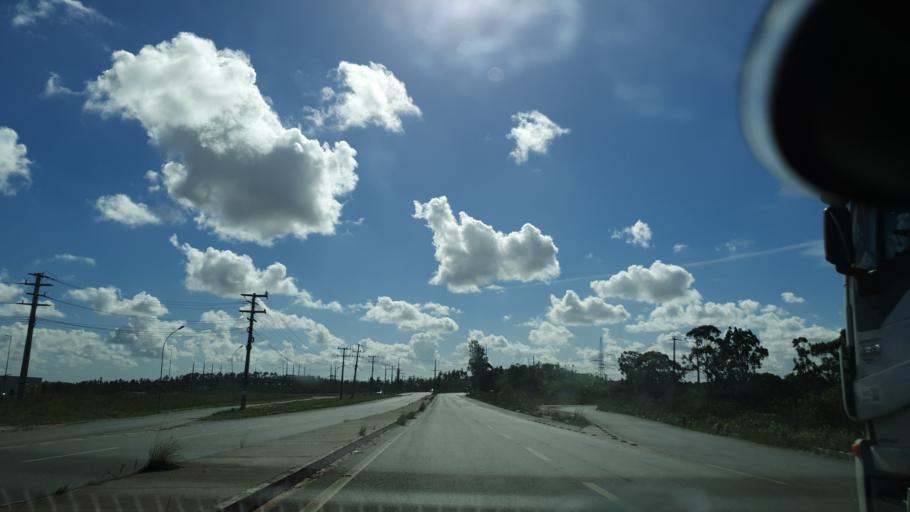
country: BR
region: Bahia
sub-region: Camacari
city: Camacari
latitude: -12.6839
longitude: -38.2679
